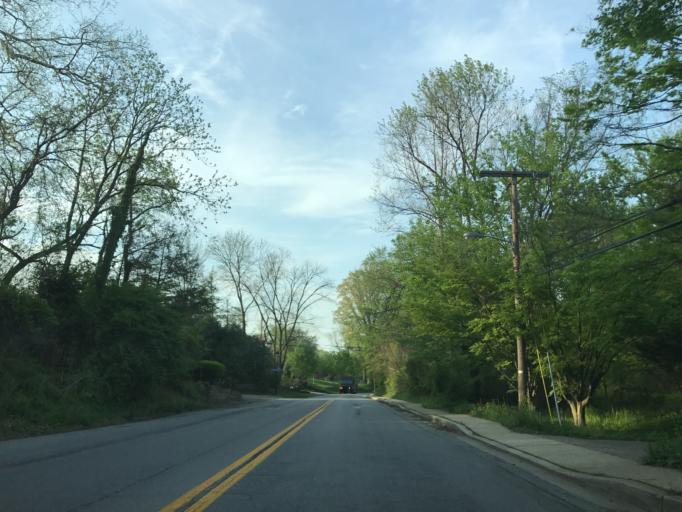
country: US
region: Maryland
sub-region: Baltimore County
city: Mays Chapel
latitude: 39.4105
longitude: -76.6488
